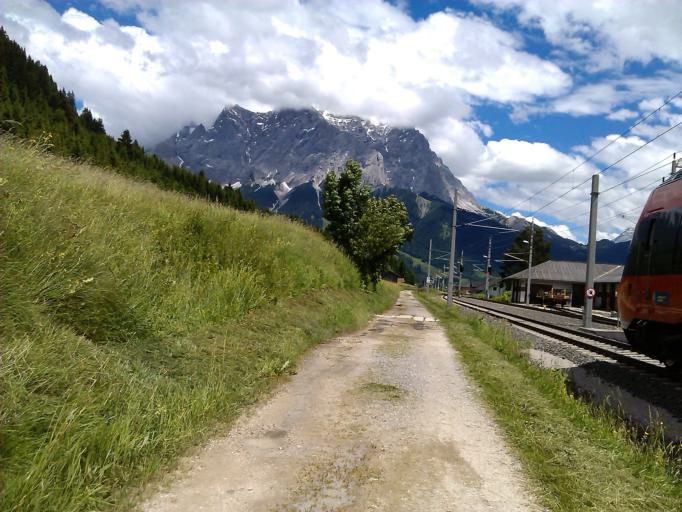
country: AT
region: Tyrol
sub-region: Politischer Bezirk Reutte
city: Lermoos
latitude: 47.4055
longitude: 10.8784
